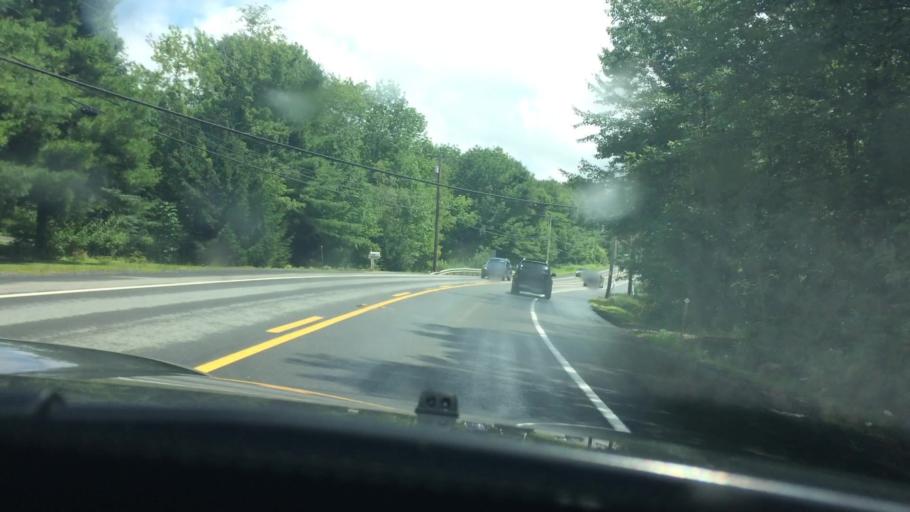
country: US
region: Massachusetts
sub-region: Worcester County
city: Phillipston
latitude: 42.5743
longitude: -72.1651
